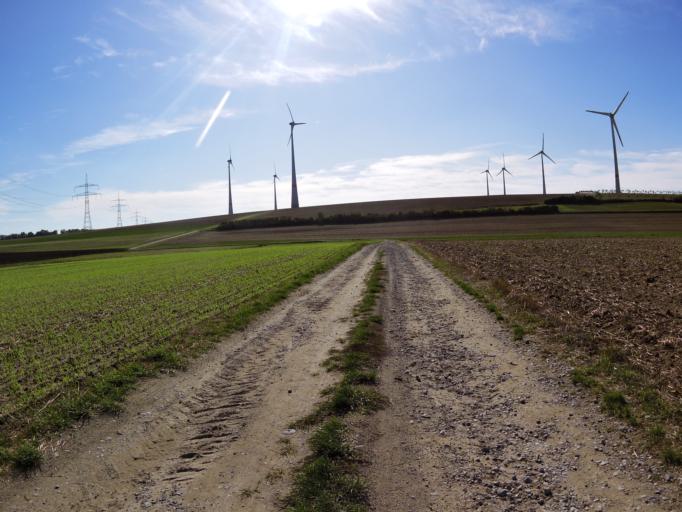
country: DE
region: Bavaria
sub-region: Regierungsbezirk Unterfranken
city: Theilheim
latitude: 49.7263
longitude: 10.0480
